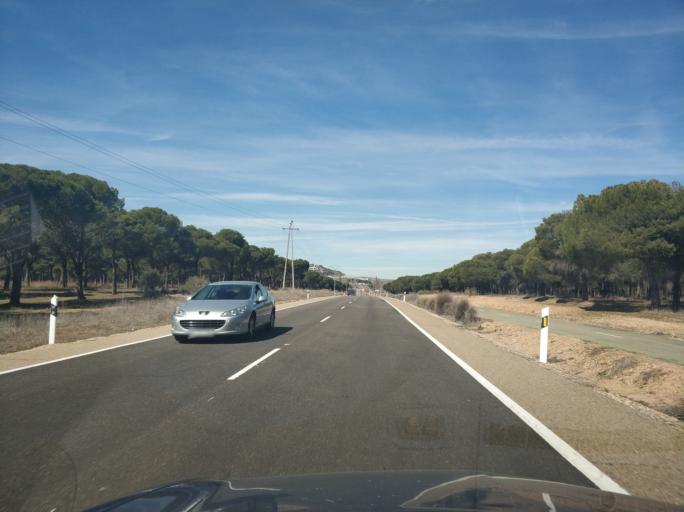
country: ES
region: Castille and Leon
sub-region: Provincia de Valladolid
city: Simancas
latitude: 41.5759
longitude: -4.8102
